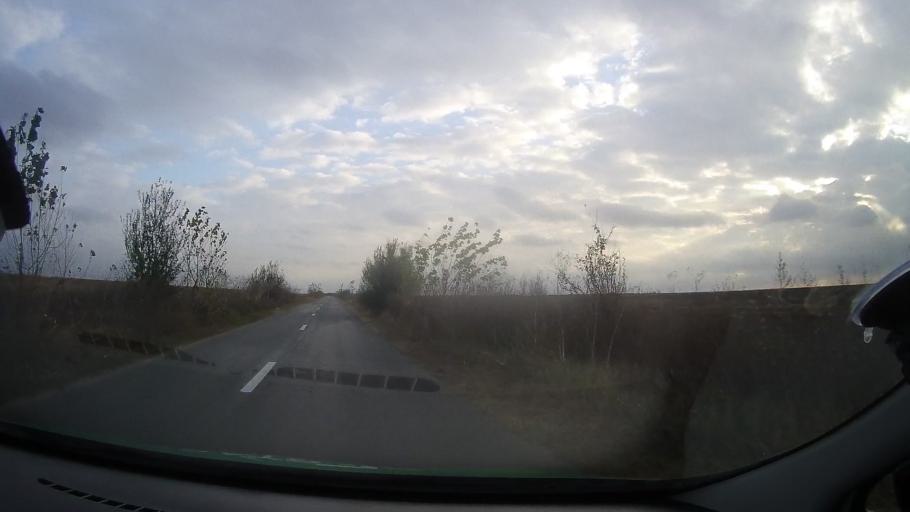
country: RO
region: Constanta
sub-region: Comuna Pestera
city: Pestera
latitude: 44.1362
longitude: 28.1185
